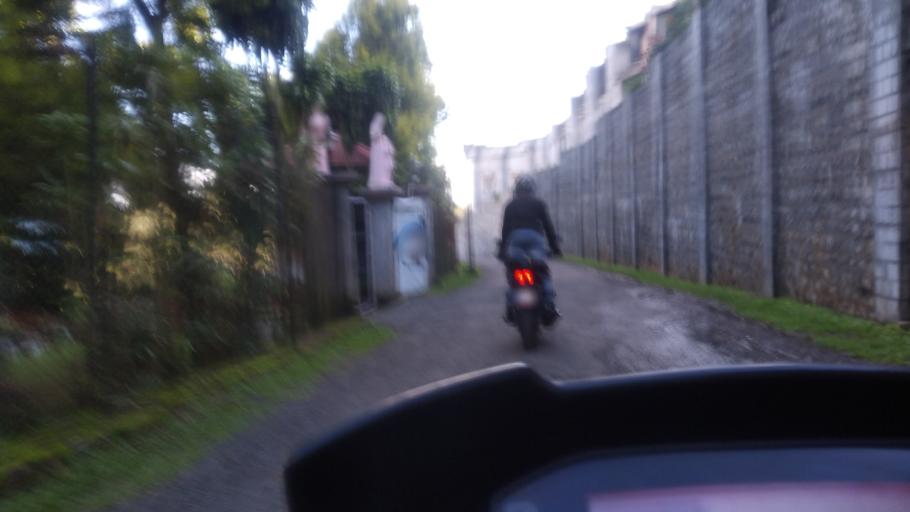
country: IN
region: Tamil Nadu
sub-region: Salem
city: Salem
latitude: 11.7714
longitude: 78.2107
